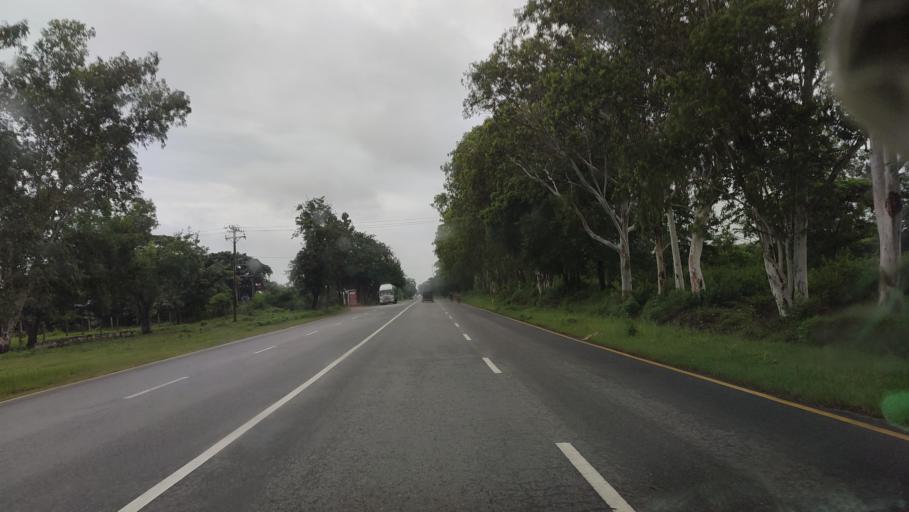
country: MM
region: Mandalay
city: Pyinmana
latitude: 19.9780
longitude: 96.2509
